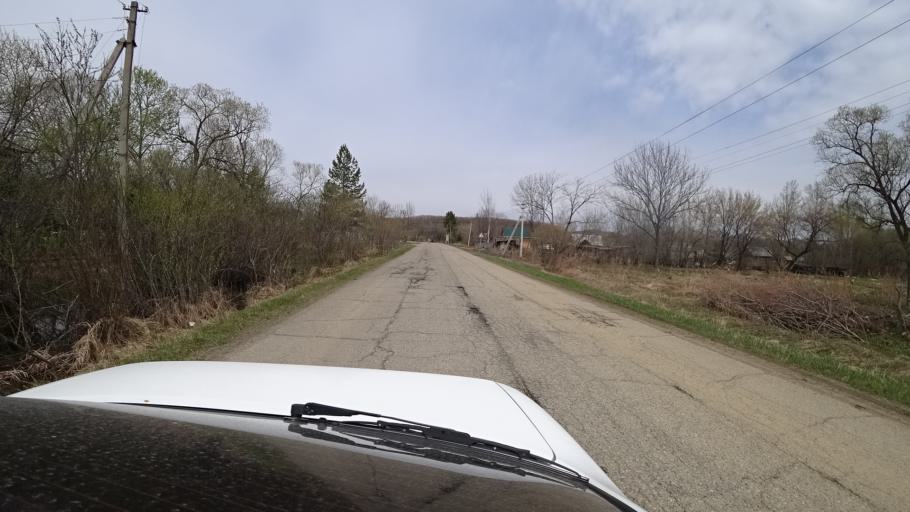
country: RU
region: Primorskiy
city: Novopokrovka
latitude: 45.7874
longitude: 134.1148
